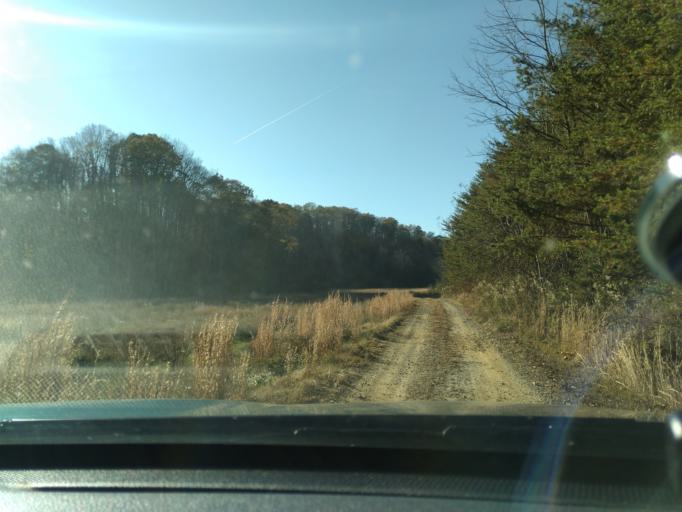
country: US
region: Virginia
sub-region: Floyd County
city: Floyd
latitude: 36.8343
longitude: -80.1817
